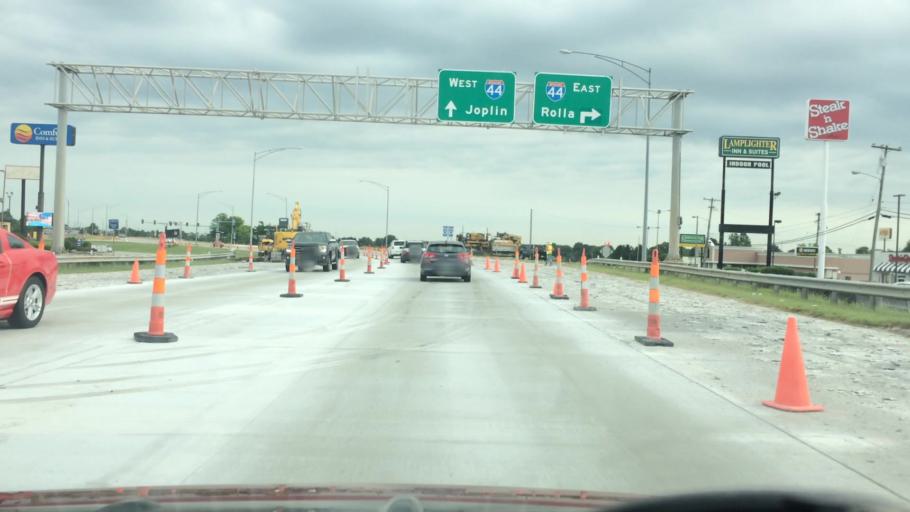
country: US
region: Missouri
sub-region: Greene County
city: Springfield
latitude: 37.2463
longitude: -93.2608
